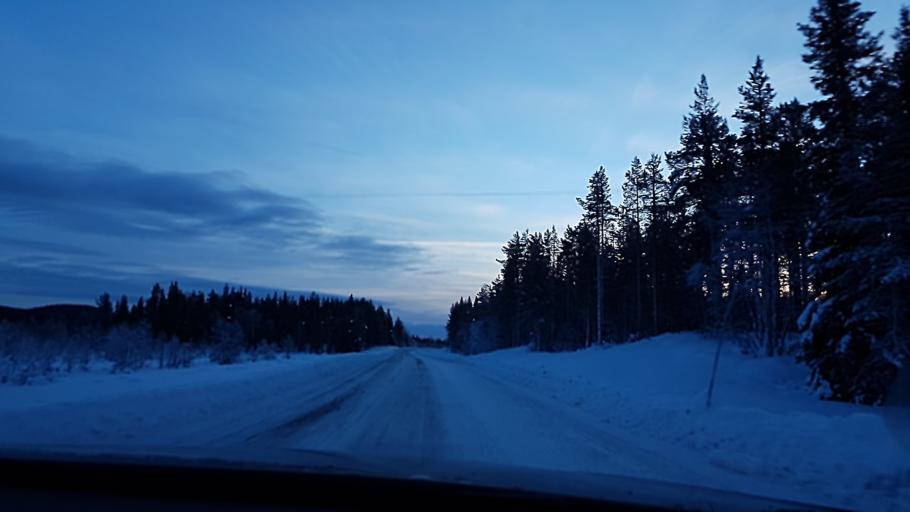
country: SE
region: Norrbotten
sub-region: Jokkmokks Kommun
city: Jokkmokk
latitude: 66.1127
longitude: 20.0441
